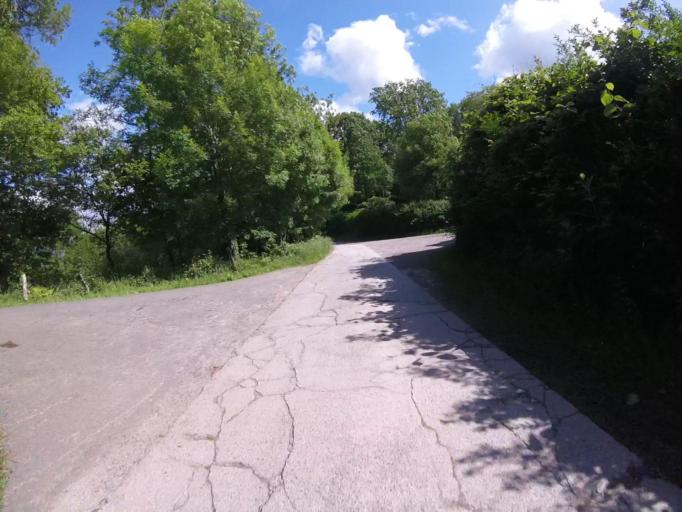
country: ES
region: Basque Country
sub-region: Provincia de Guipuzcoa
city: Errenteria
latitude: 43.2931
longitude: -1.9120
